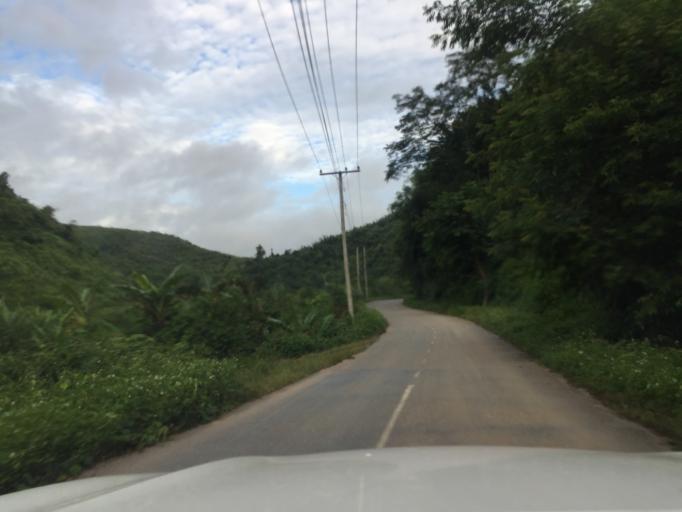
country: LA
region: Phongsali
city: Khoa
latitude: 21.1010
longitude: 102.2810
